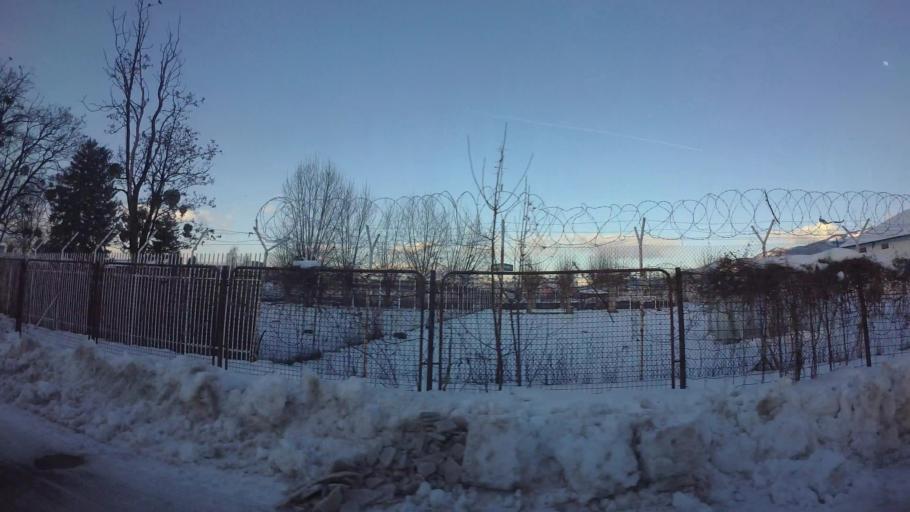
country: BA
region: Federation of Bosnia and Herzegovina
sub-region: Kanton Sarajevo
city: Sarajevo
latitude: 43.8146
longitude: 18.3561
